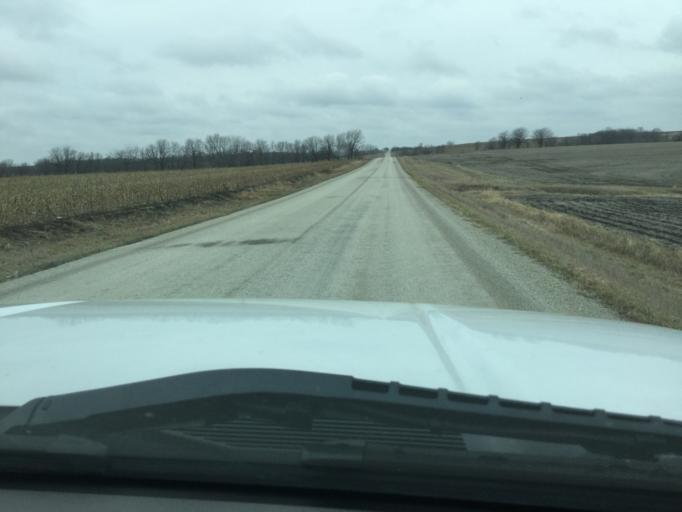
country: US
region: Kansas
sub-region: Nemaha County
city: Sabetha
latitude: 39.7979
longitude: -95.7344
